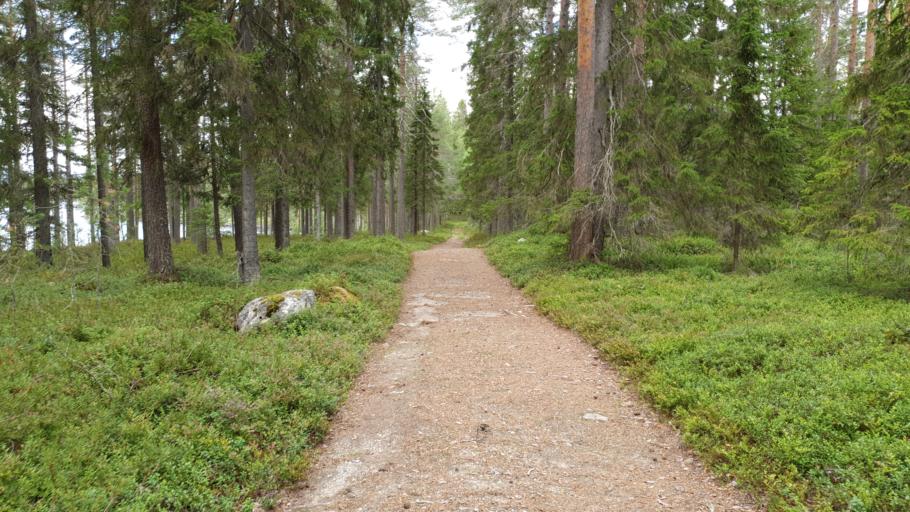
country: FI
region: Kainuu
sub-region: Kehys-Kainuu
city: Kuhmo
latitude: 64.3819
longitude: 29.8049
